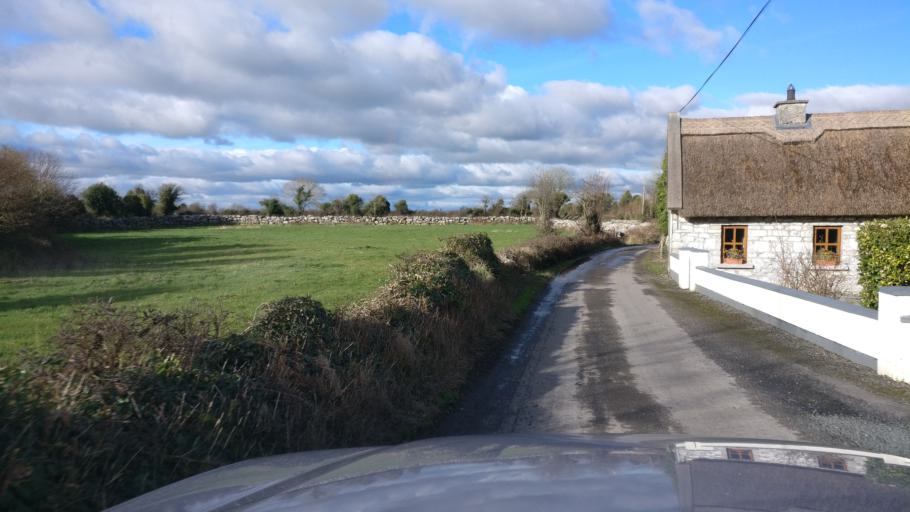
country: IE
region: Connaught
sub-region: County Galway
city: Athenry
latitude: 53.2287
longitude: -8.7994
